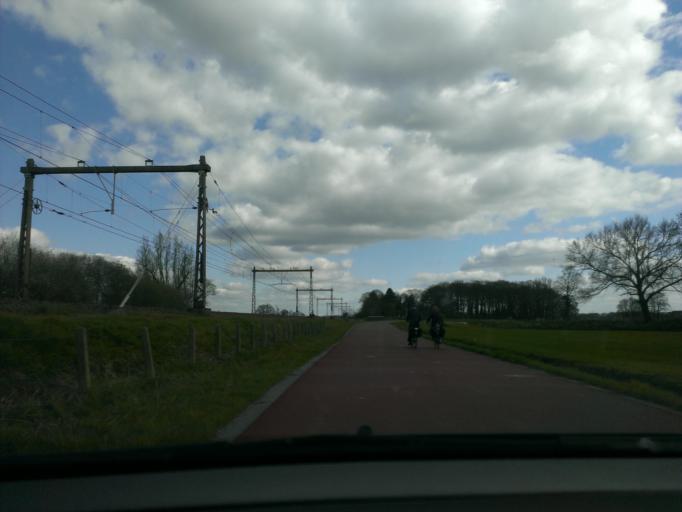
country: NL
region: Overijssel
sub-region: Gemeente Borne
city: Borne
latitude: 52.3187
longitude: 6.7116
